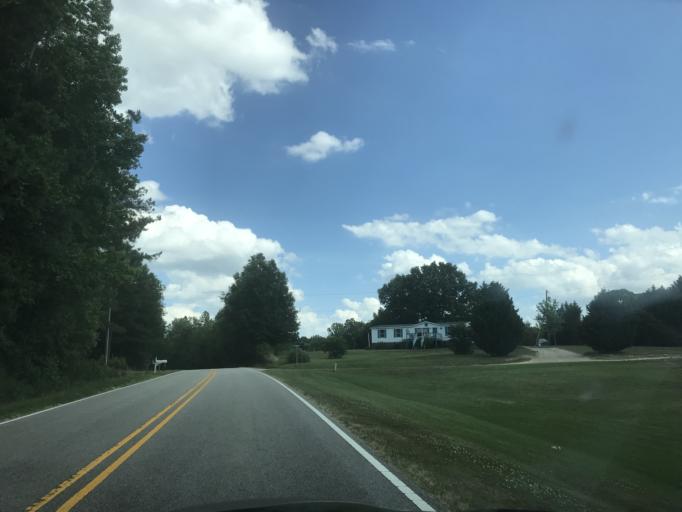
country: US
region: North Carolina
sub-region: Nash County
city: Spring Hope
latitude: 35.9346
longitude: -78.2051
